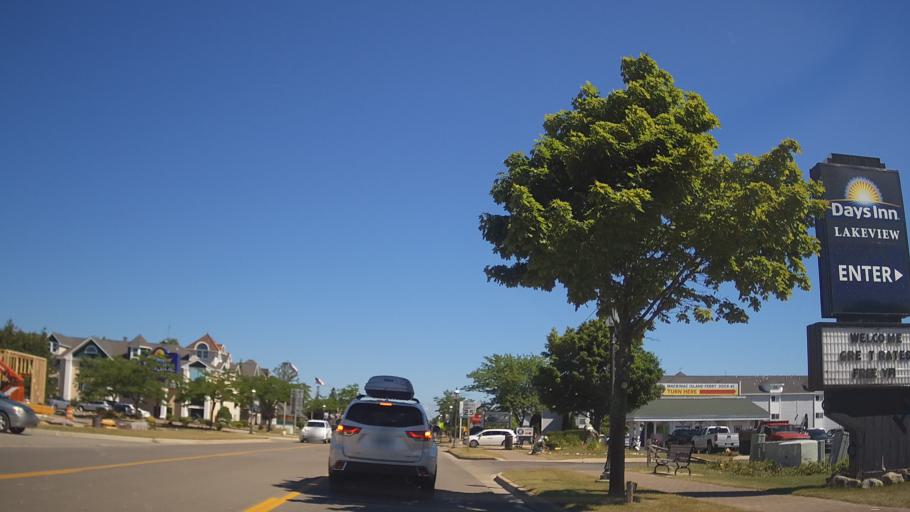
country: US
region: Michigan
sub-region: Mackinac County
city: Saint Ignace
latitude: 45.7719
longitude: -84.7268
